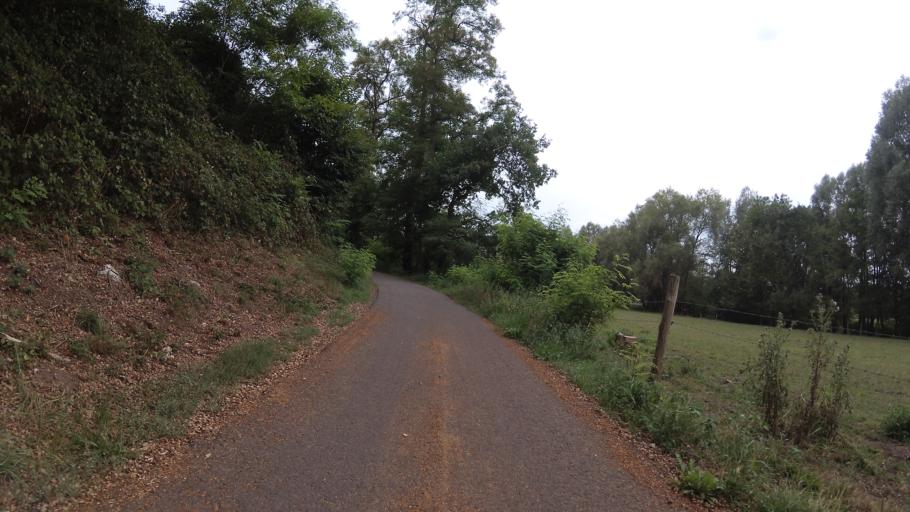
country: DE
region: Saarland
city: Homburg
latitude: 49.3053
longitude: 7.3053
